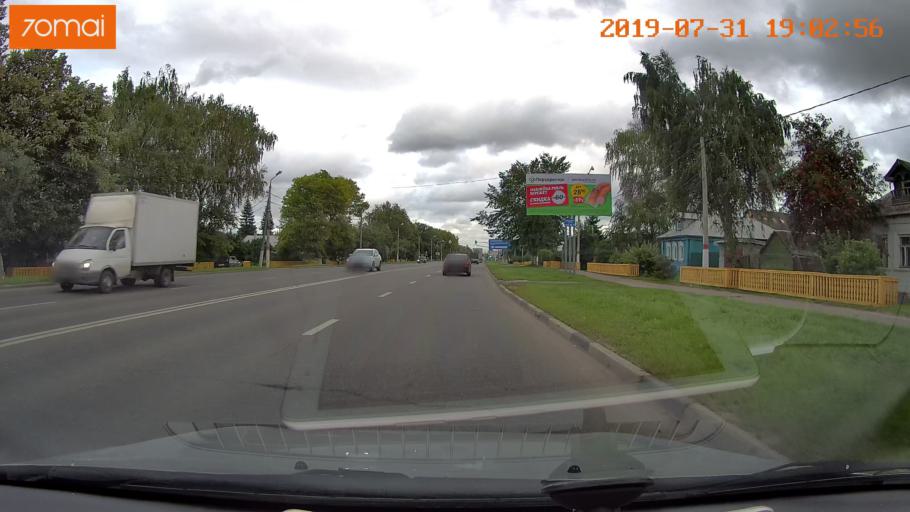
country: RU
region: Moskovskaya
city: Raduzhnyy
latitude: 55.1178
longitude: 38.7355
